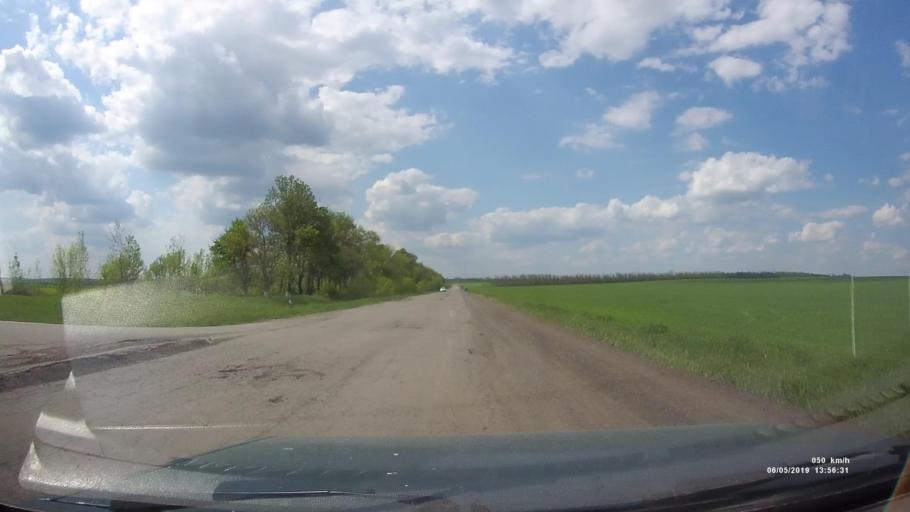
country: RU
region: Rostov
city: Melikhovskaya
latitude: 47.6812
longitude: 40.4303
